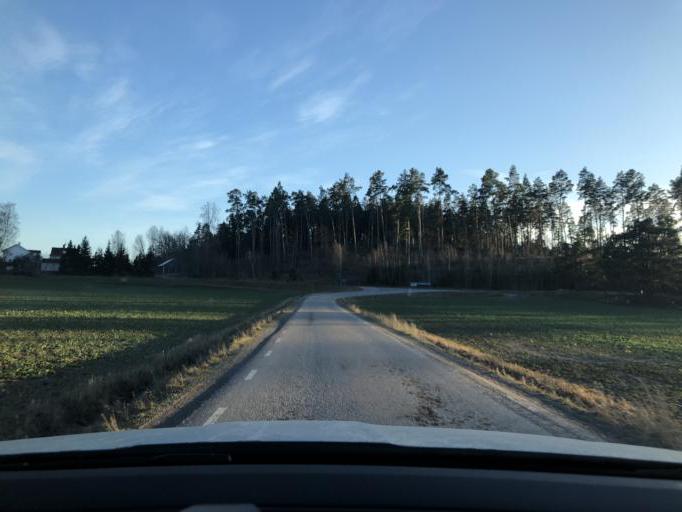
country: SE
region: Soedermanland
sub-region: Eskilstuna Kommun
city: Arla
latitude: 59.4282
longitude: 16.6472
